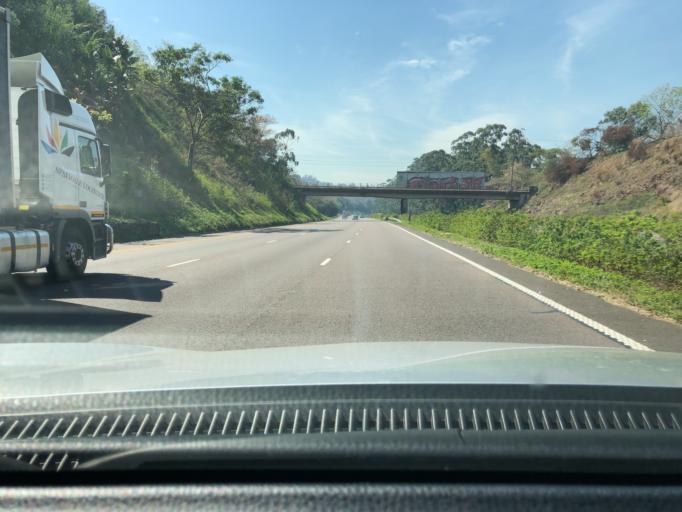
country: ZA
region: KwaZulu-Natal
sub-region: eThekwini Metropolitan Municipality
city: Berea
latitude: -29.8370
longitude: 30.8752
